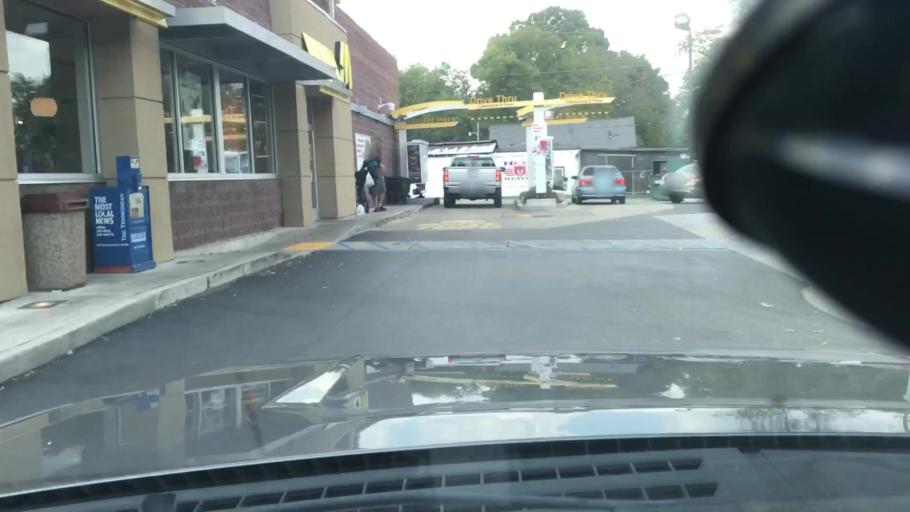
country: US
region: Tennessee
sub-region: Davidson County
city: Nashville
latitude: 36.1459
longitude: -86.8119
